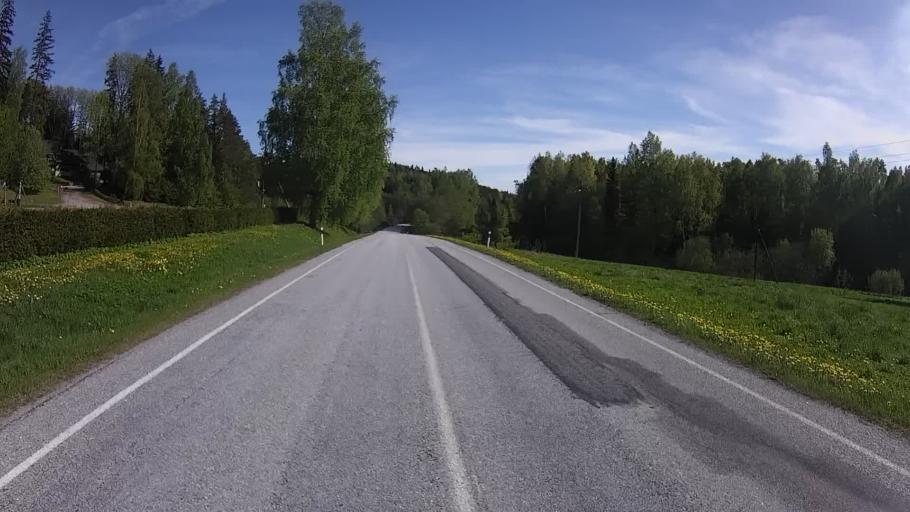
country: EE
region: Vorumaa
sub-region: Antsla vald
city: Vana-Antsla
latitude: 58.0366
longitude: 26.5082
